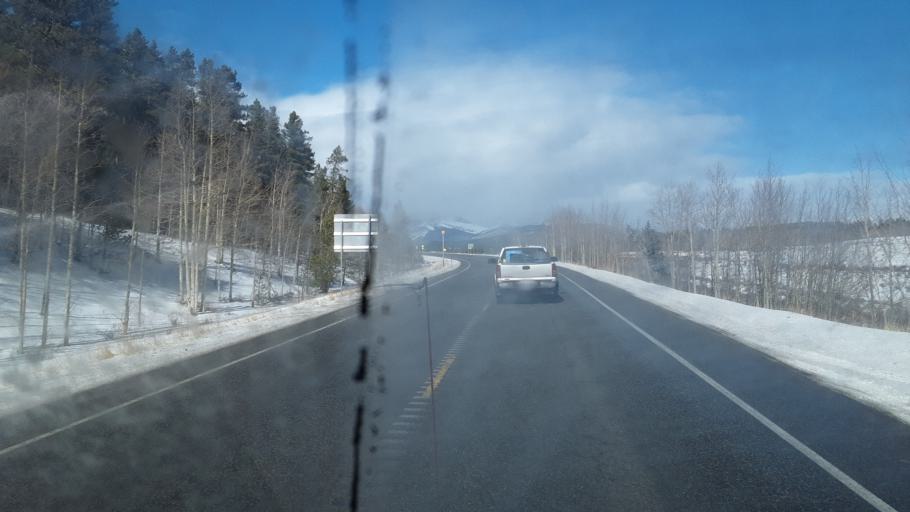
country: US
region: Colorado
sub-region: Summit County
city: Breckenridge
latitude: 39.4091
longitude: -105.7561
